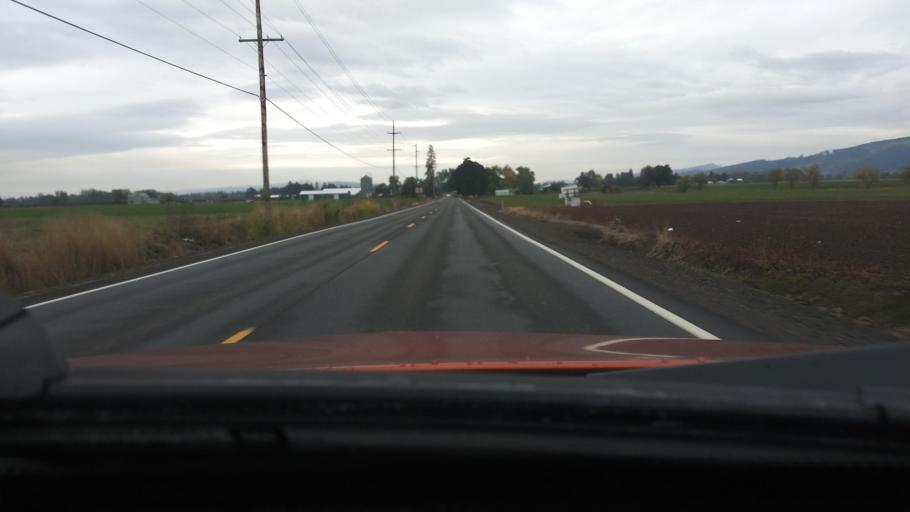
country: US
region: Oregon
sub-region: Washington County
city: Banks
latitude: 45.5918
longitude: -123.1144
